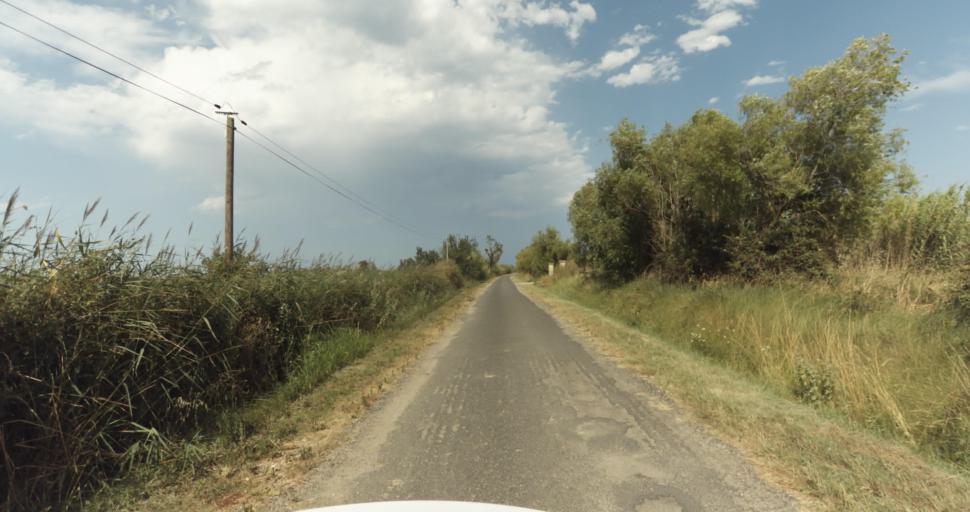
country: FR
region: Languedoc-Roussillon
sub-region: Departement des Pyrenees-Orientales
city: Alenya
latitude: 42.6462
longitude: 2.9936
